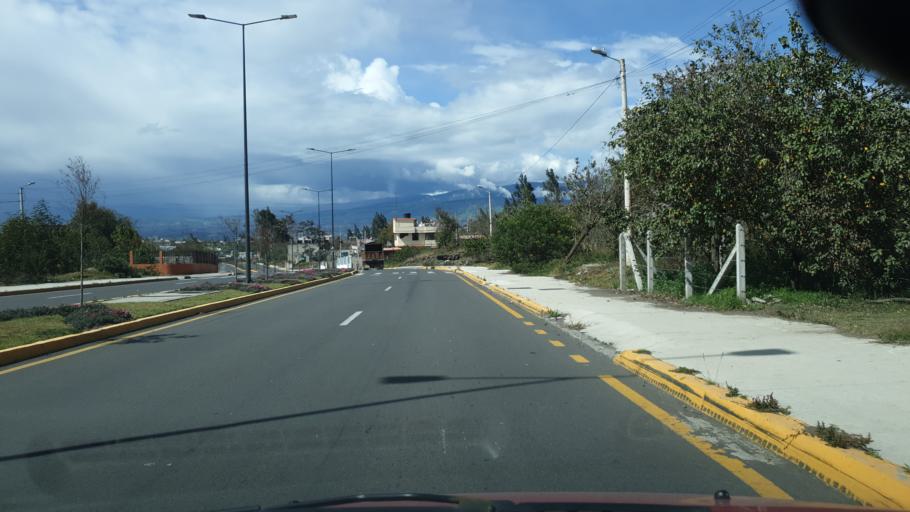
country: EC
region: Tungurahua
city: Ambato
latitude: -1.2953
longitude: -78.6340
